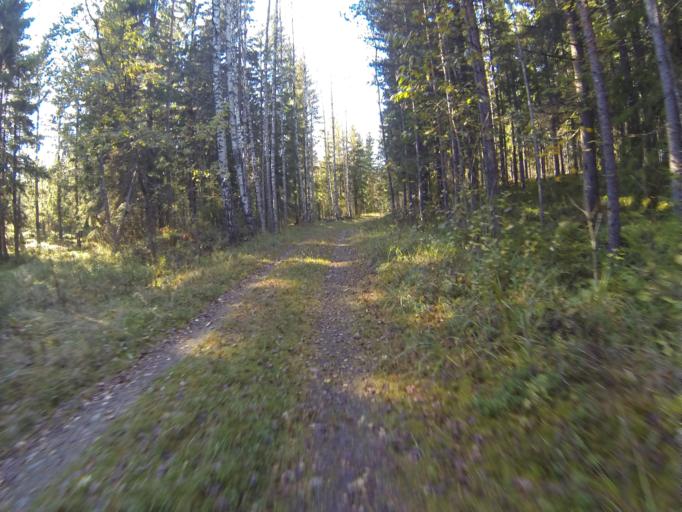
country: FI
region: Varsinais-Suomi
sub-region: Salo
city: Saerkisalo
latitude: 60.2251
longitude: 22.9746
